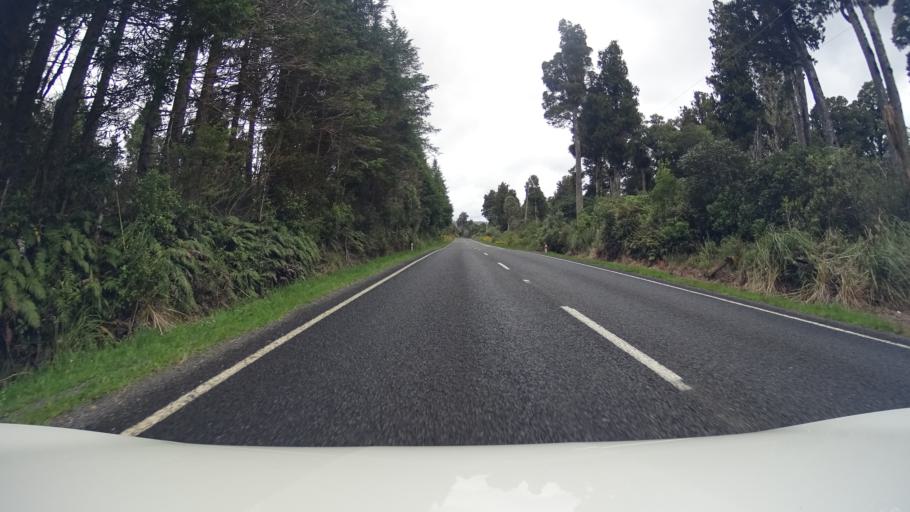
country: NZ
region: Manawatu-Wanganui
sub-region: Ruapehu District
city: Waiouru
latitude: -39.2396
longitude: 175.3917
